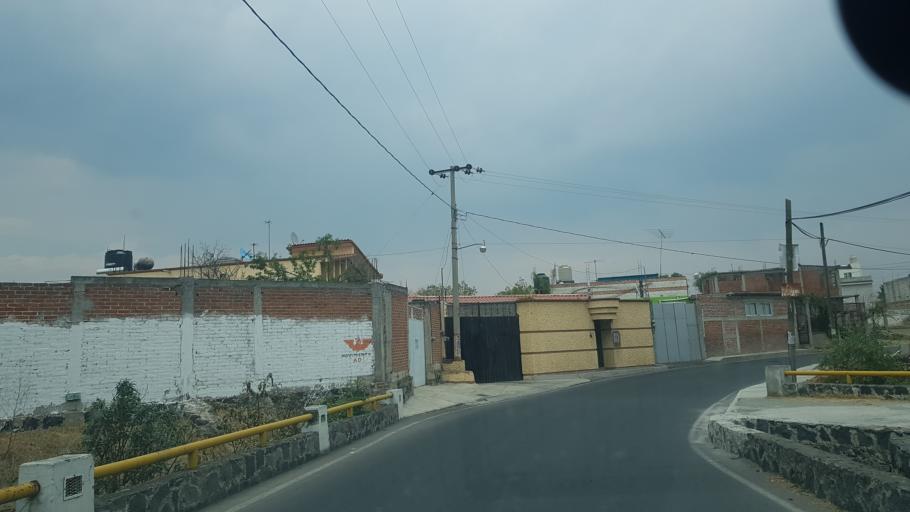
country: MX
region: Puebla
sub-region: Huejotzingo
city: San Mateo Capultitlan
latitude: 19.2003
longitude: -98.4393
